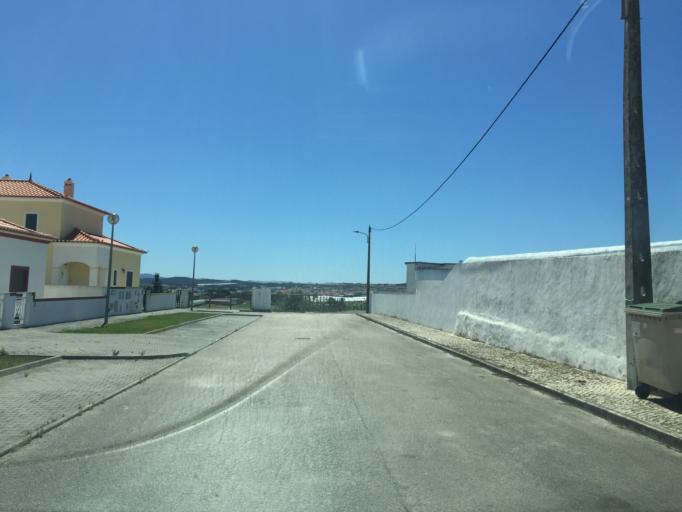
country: PT
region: Lisbon
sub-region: Torres Vedras
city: A dos Cunhados
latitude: 39.1753
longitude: -9.3158
